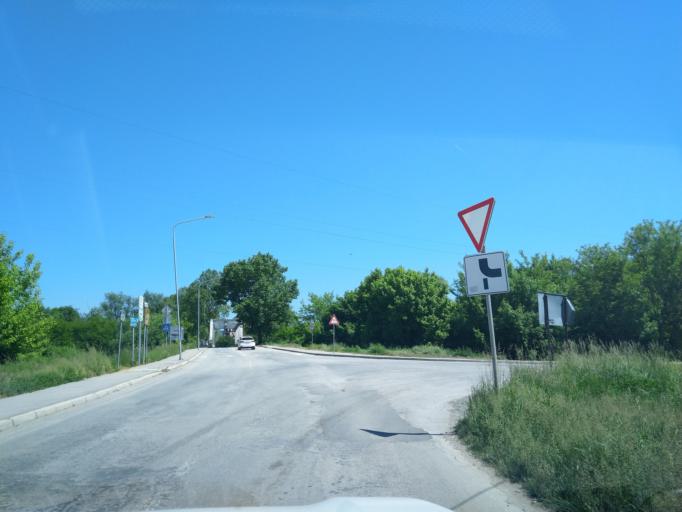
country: RS
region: Central Serbia
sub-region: Zlatiborski Okrug
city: Pozega
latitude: 43.8447
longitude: 20.0267
